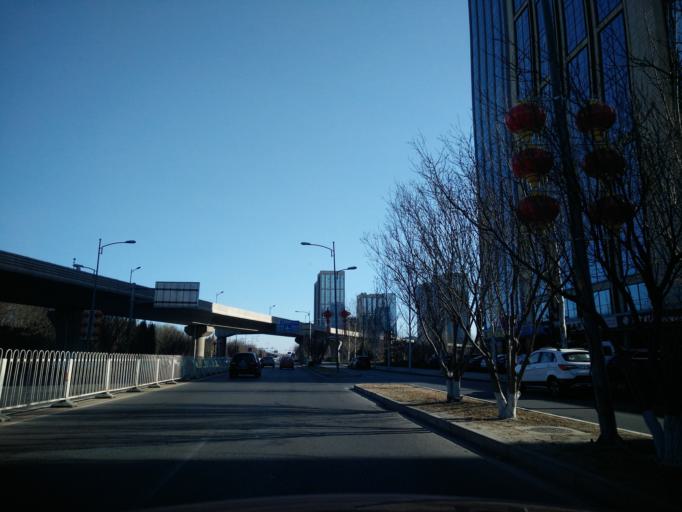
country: CN
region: Beijing
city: Jiugong
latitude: 39.8062
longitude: 116.4872
